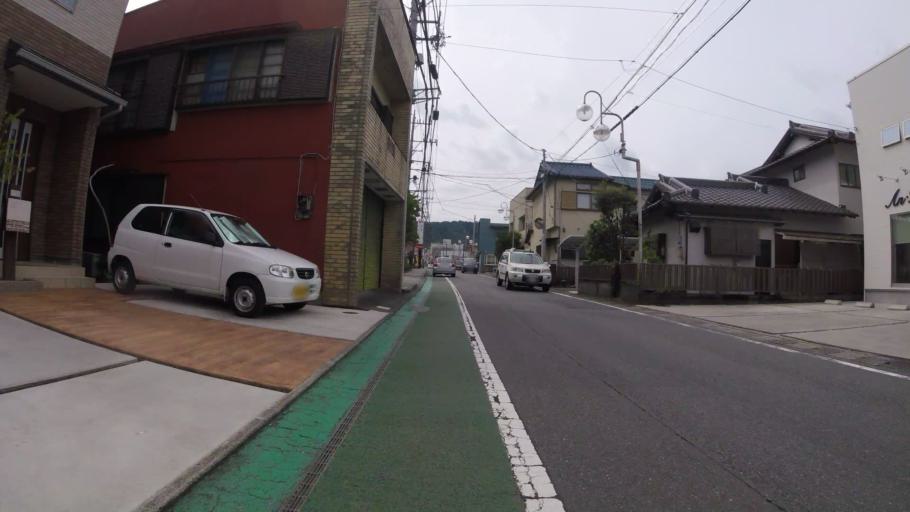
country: JP
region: Shizuoka
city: Mishima
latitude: 34.9972
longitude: 138.9390
